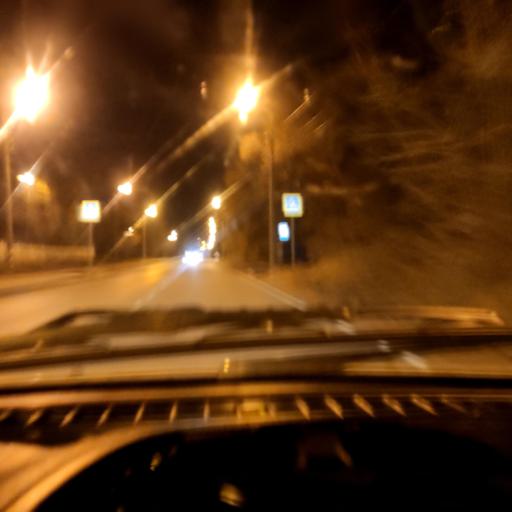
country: RU
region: Samara
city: Zhigulevsk
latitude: 53.4645
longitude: 49.5413
